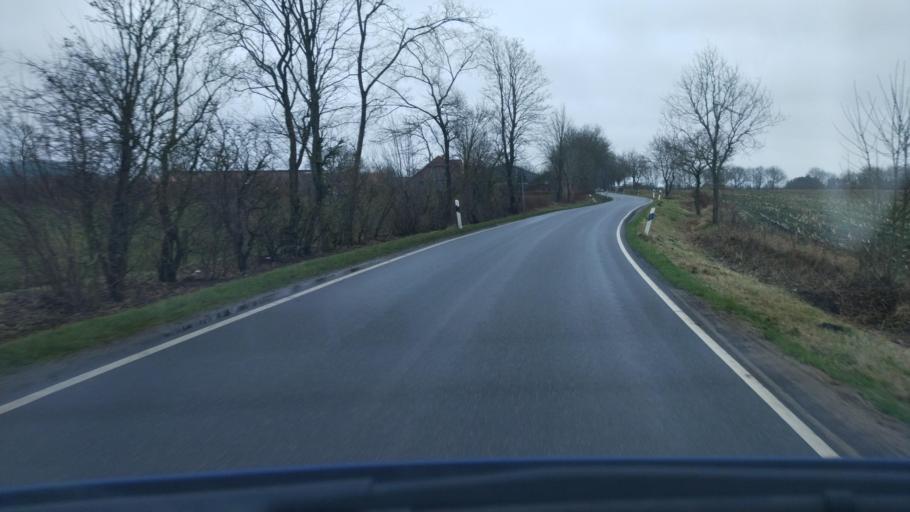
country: DE
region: Schleswig-Holstein
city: Gross Rheide
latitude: 54.4499
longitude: 9.4136
